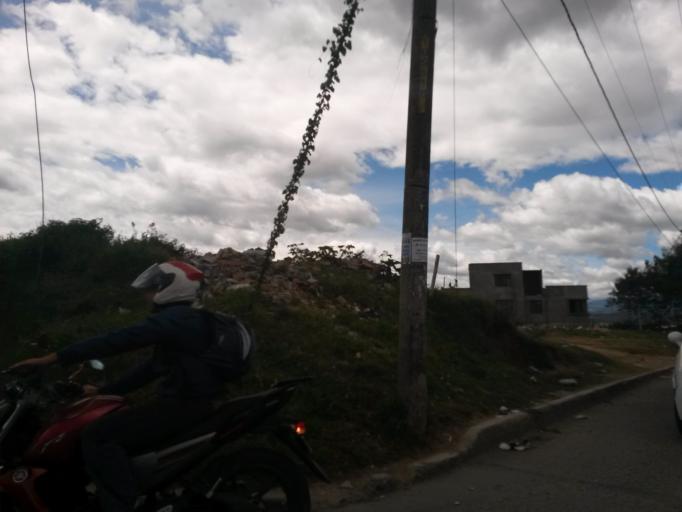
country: CO
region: Cauca
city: Popayan
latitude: 2.4383
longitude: -76.6217
